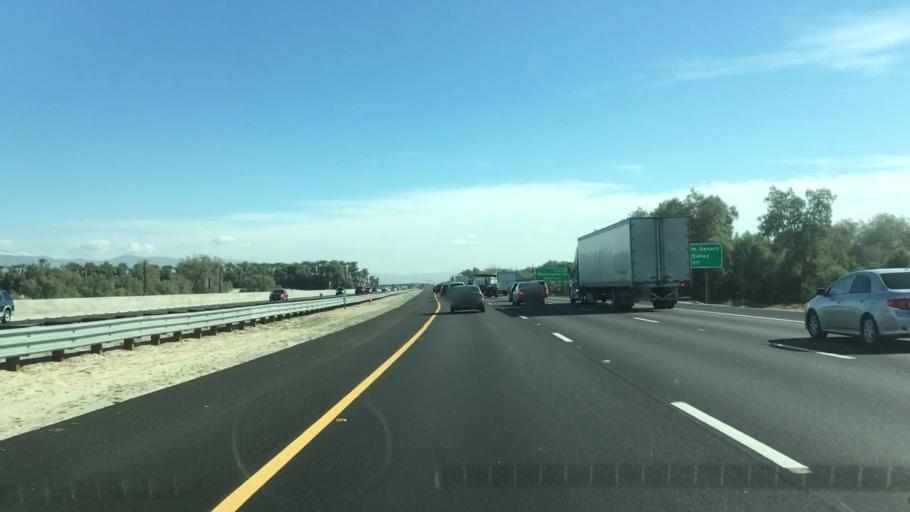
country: US
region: California
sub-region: Riverside County
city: Bermuda Dunes
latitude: 33.7648
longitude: -116.3178
